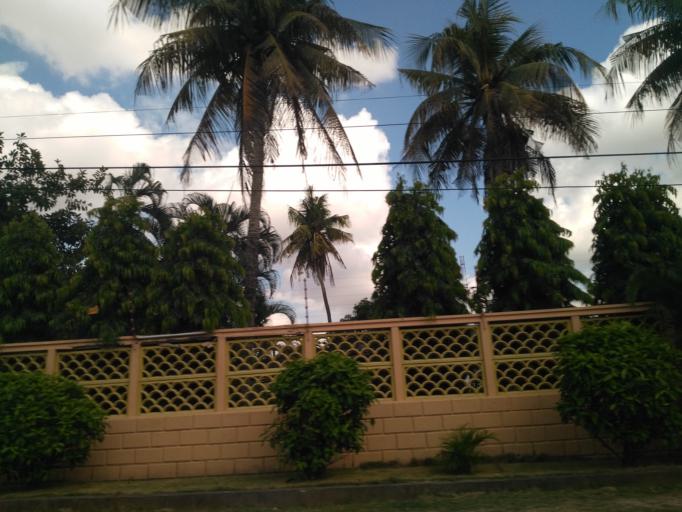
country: TZ
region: Dar es Salaam
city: Magomeni
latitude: -6.7582
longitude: 39.2445
